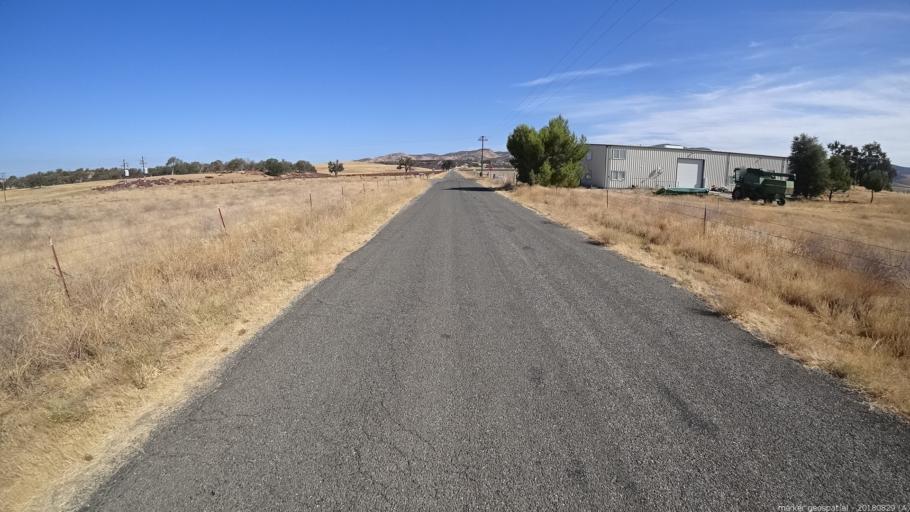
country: US
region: California
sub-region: Monterey County
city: King City
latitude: 35.9656
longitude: -121.1175
